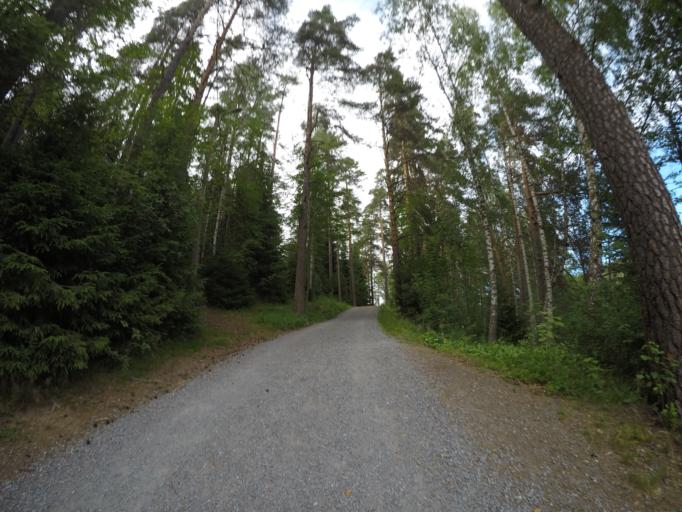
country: FI
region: Haeme
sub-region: Haemeenlinna
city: Haemeenlinna
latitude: 60.9932
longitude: 24.4182
